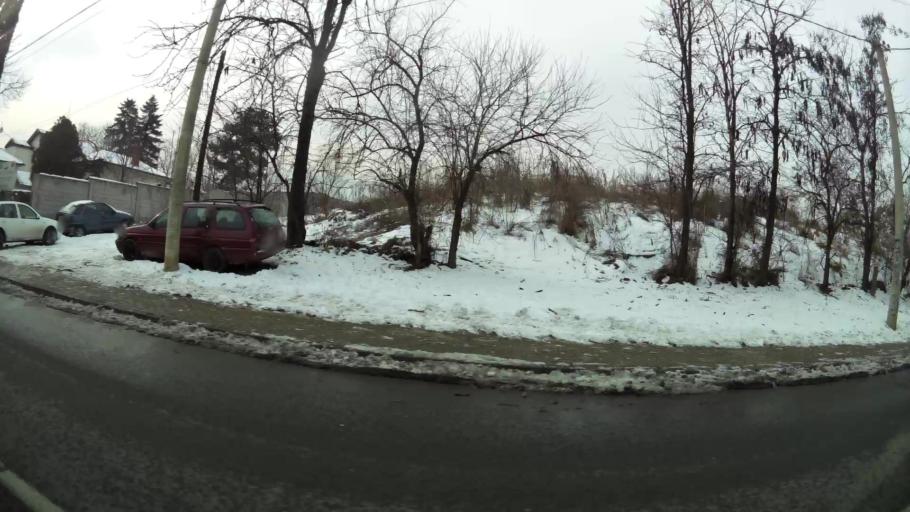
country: MK
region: Karpos
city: Skopje
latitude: 42.0072
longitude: 21.4321
